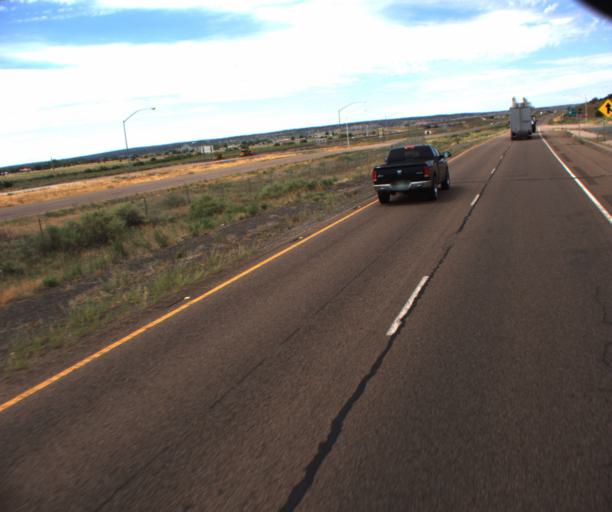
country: US
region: Arizona
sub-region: Apache County
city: Houck
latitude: 35.2228
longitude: -109.3225
